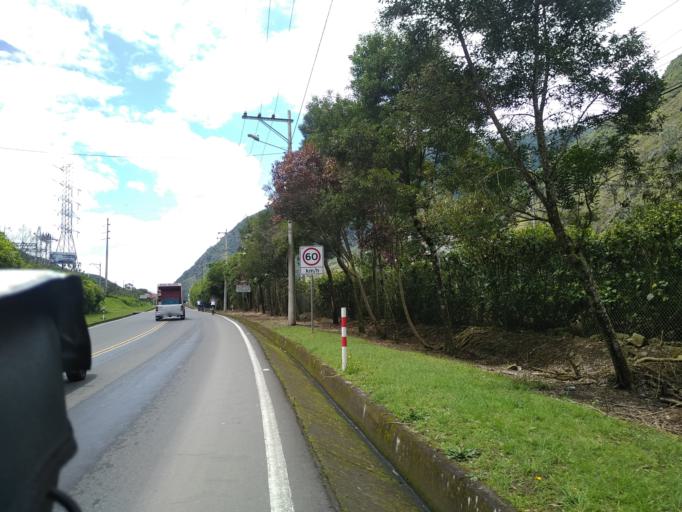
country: EC
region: Tungurahua
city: Banos
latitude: -1.3980
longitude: -78.3780
